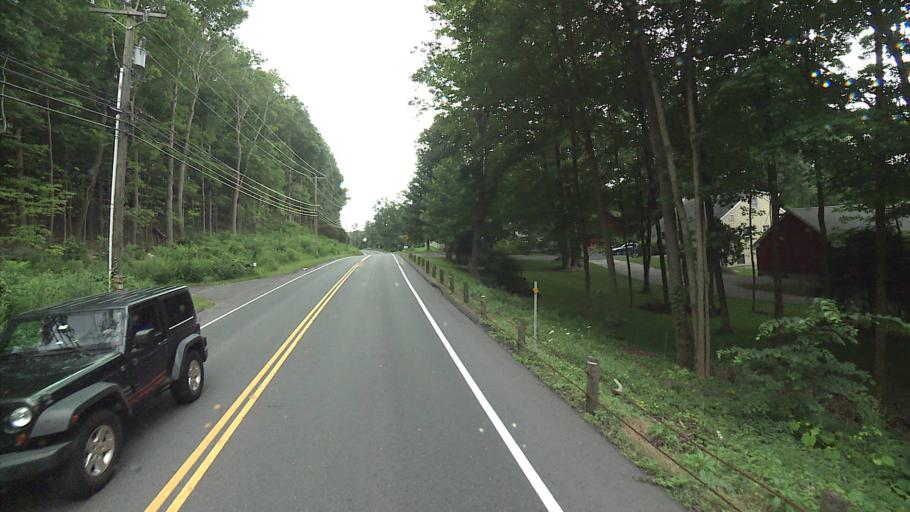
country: US
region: Connecticut
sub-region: New Haven County
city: Southbury
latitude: 41.4702
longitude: -73.1792
